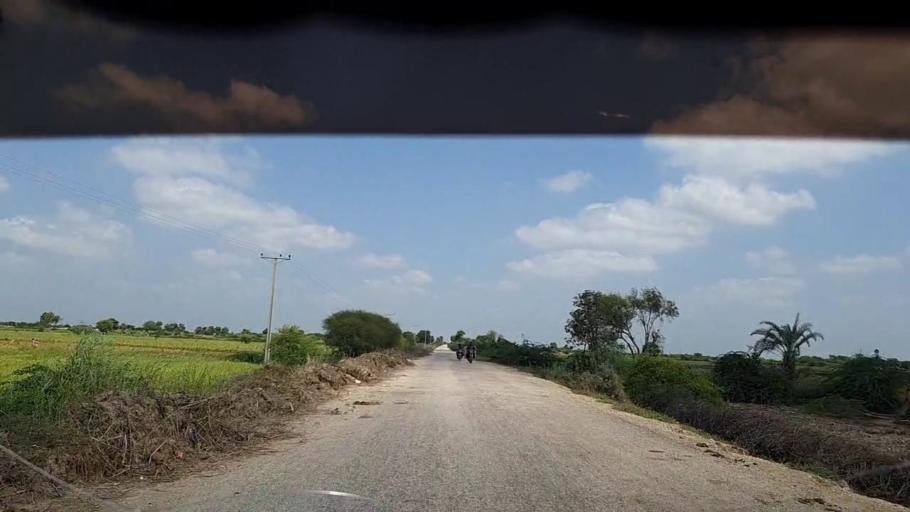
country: PK
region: Sindh
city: Kadhan
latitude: 24.5961
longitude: 68.9631
